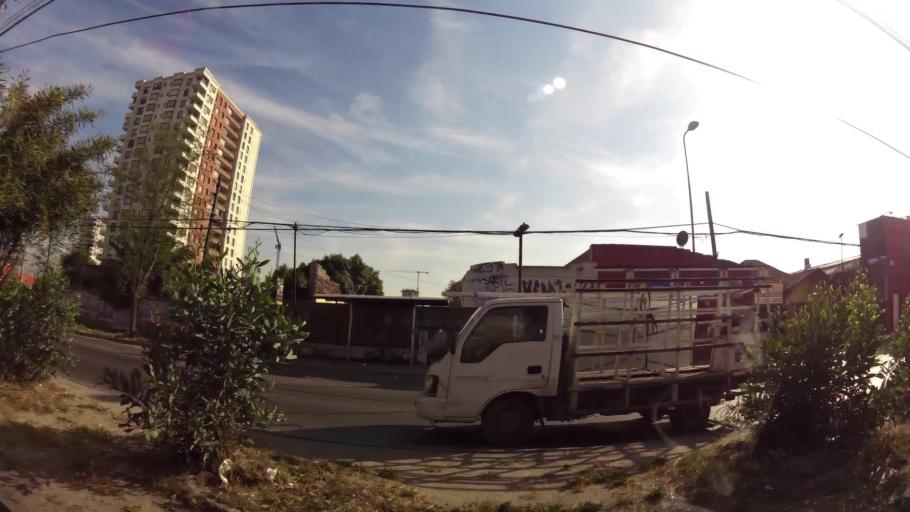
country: CL
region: Santiago Metropolitan
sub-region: Provincia de Santiago
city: Santiago
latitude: -33.5043
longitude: -70.6516
